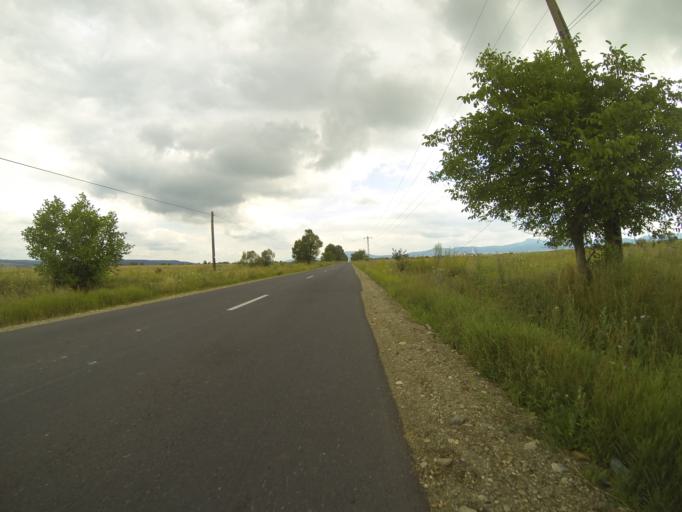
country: RO
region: Brasov
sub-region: Comuna Parau
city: Parau
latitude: 45.8428
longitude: 25.1701
